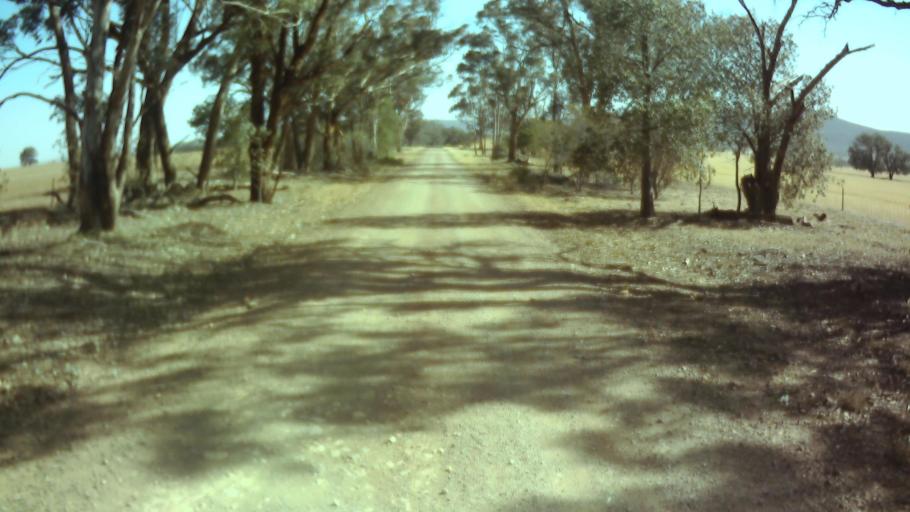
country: AU
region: New South Wales
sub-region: Weddin
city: Grenfell
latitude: -33.8504
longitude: 148.0165
